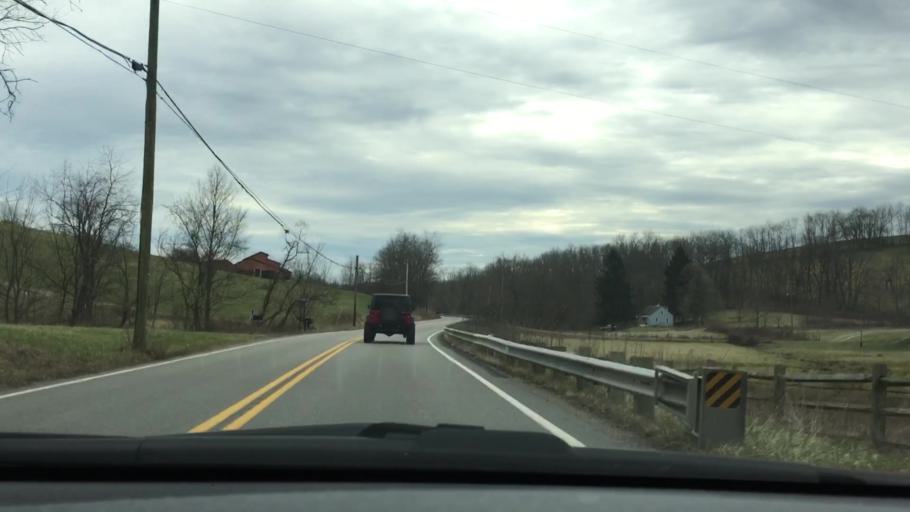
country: US
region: Pennsylvania
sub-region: Washington County
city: Muse
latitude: 40.2980
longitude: -80.2188
